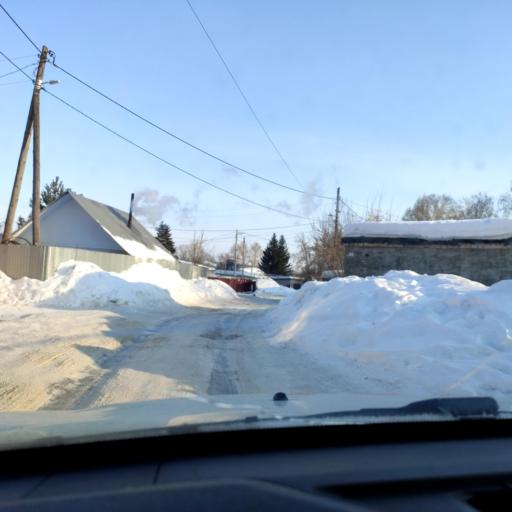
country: RU
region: Samara
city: Petra-Dubrava
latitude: 53.3192
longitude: 50.2894
